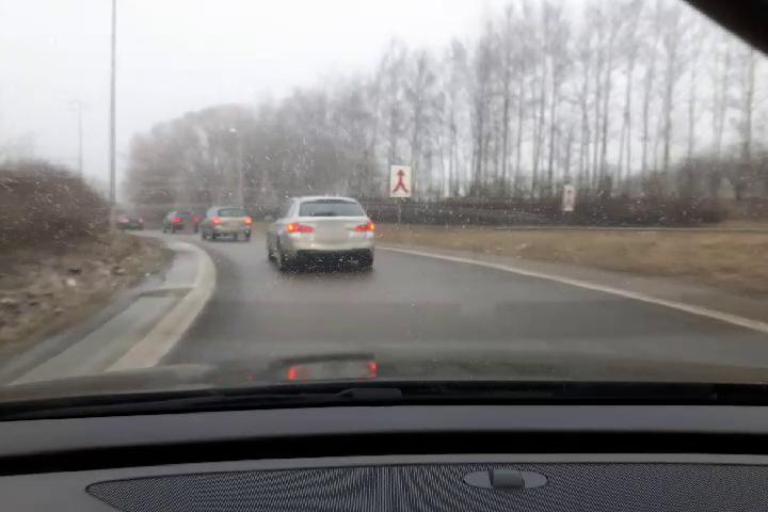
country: SE
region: Vaestra Goetaland
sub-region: Goteborg
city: Goeteborg
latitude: 57.7210
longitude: 11.9889
